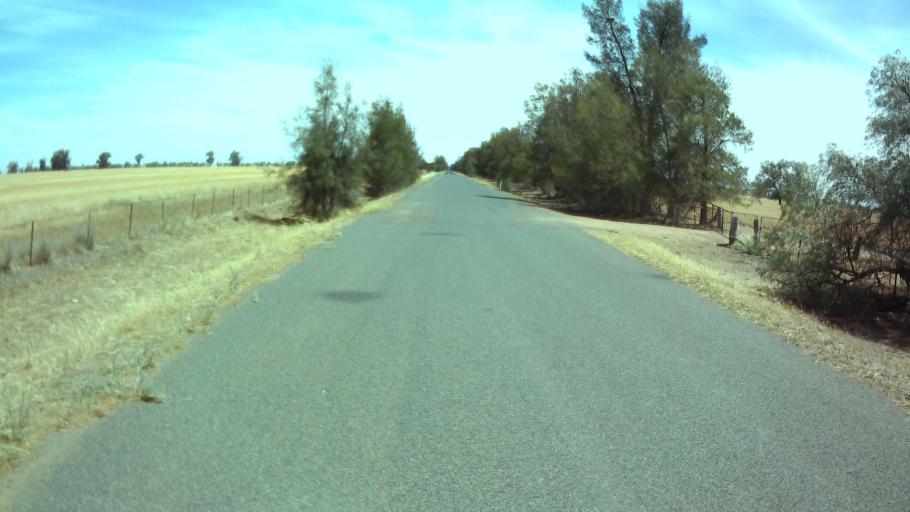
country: AU
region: New South Wales
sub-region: Weddin
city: Grenfell
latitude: -33.9159
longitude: 147.7651
